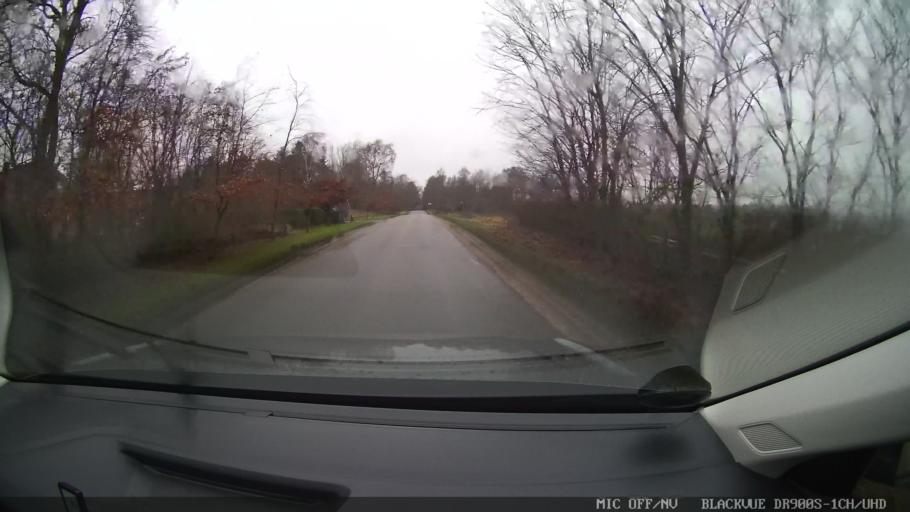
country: DK
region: Central Jutland
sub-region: Viborg Kommune
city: Karup
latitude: 56.2898
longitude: 9.1633
